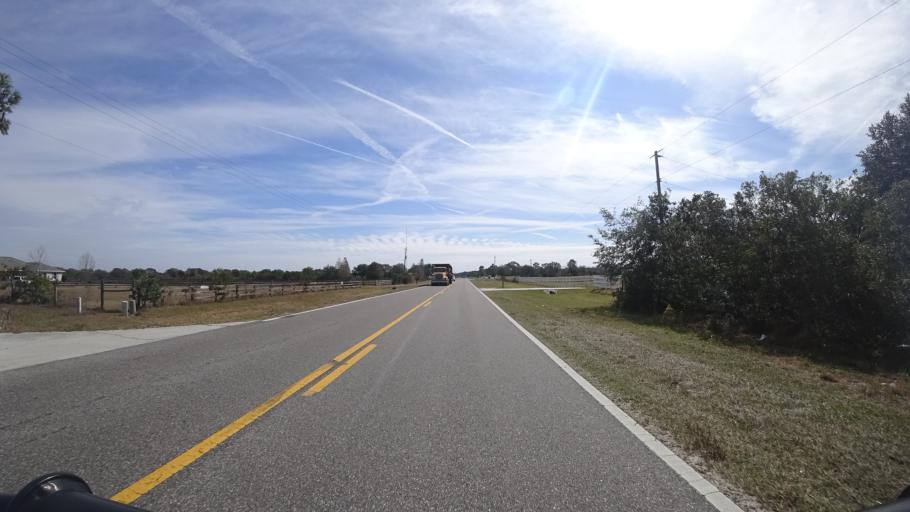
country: US
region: Florida
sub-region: Hillsborough County
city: Sun City Center
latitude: 27.5676
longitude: -82.3800
